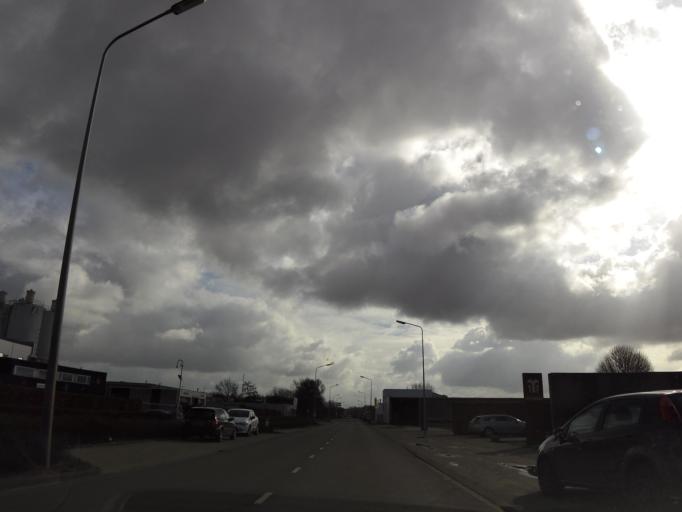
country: NL
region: Limburg
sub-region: Gemeente Maastricht
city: Maastricht
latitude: 50.8756
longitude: 5.7070
